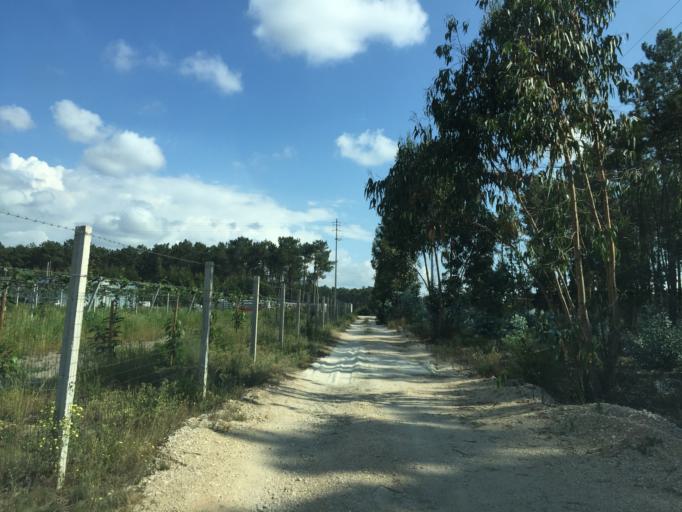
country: PT
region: Leiria
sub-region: Leiria
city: Monte Redondo
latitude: 39.9442
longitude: -8.8255
